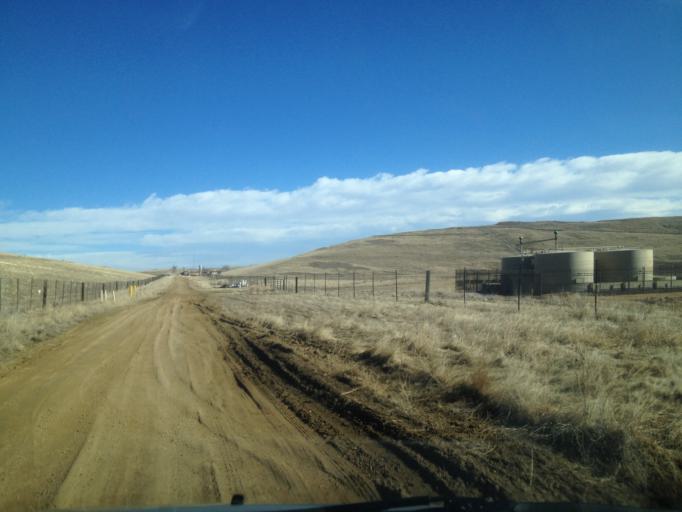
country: US
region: Colorado
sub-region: Boulder County
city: Erie
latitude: 40.0293
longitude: -105.0363
